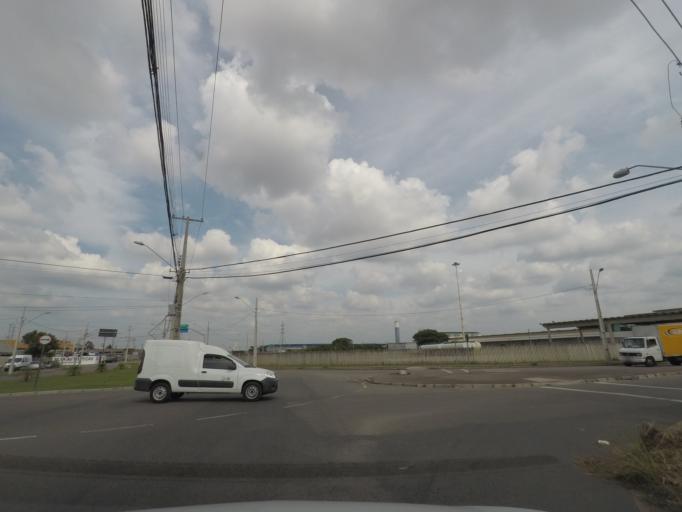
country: BR
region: Parana
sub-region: Sao Jose Dos Pinhais
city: Sao Jose dos Pinhais
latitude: -25.4997
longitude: -49.2124
